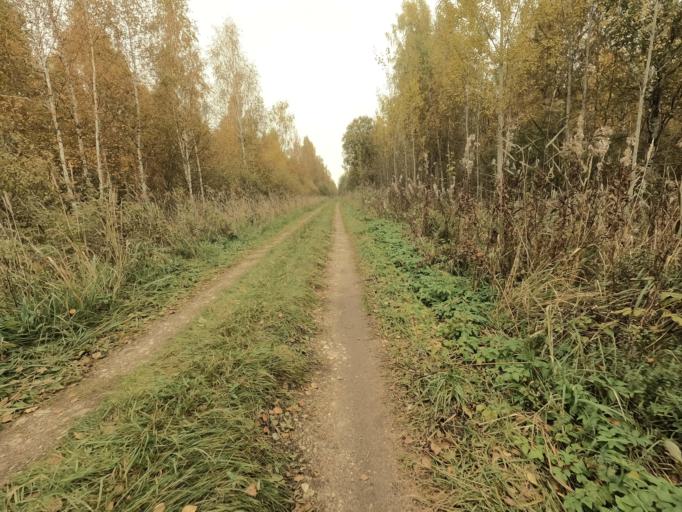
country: RU
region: Novgorod
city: Pankovka
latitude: 58.8886
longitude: 30.9483
